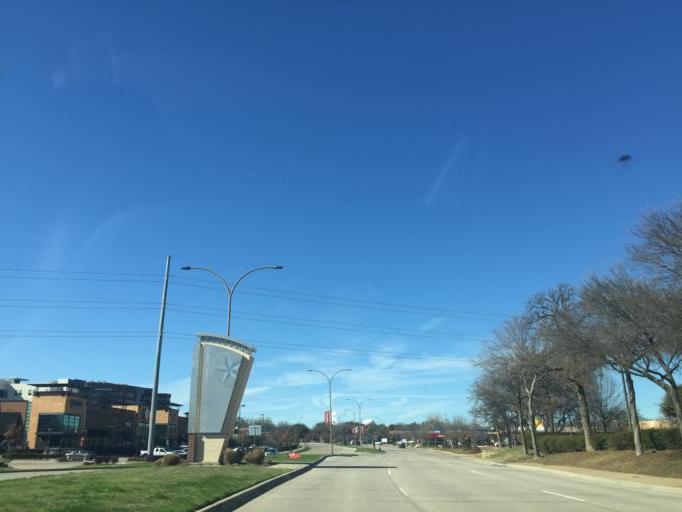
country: US
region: Texas
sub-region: Tarrant County
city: Arlington
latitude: 32.7616
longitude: -97.0725
